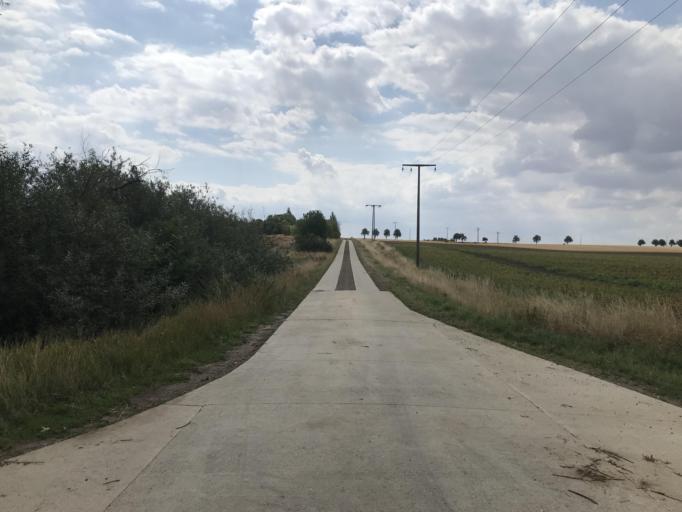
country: DE
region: Lower Saxony
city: Sollingen
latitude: 52.0348
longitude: 10.9533
